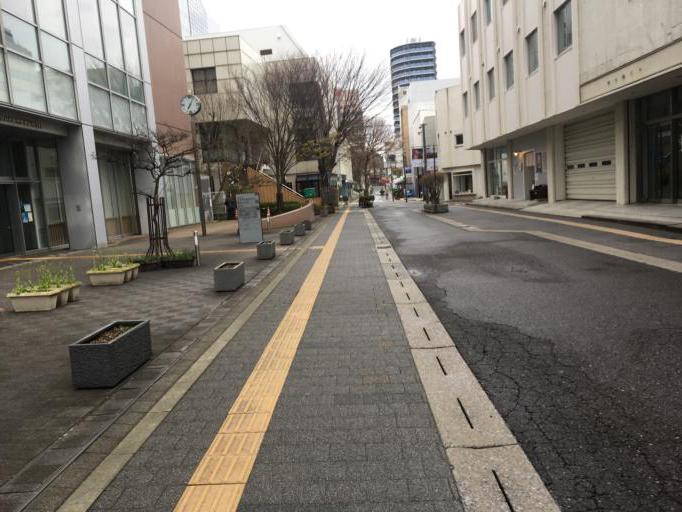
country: JP
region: Akita
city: Akita
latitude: 39.7173
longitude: 140.1223
